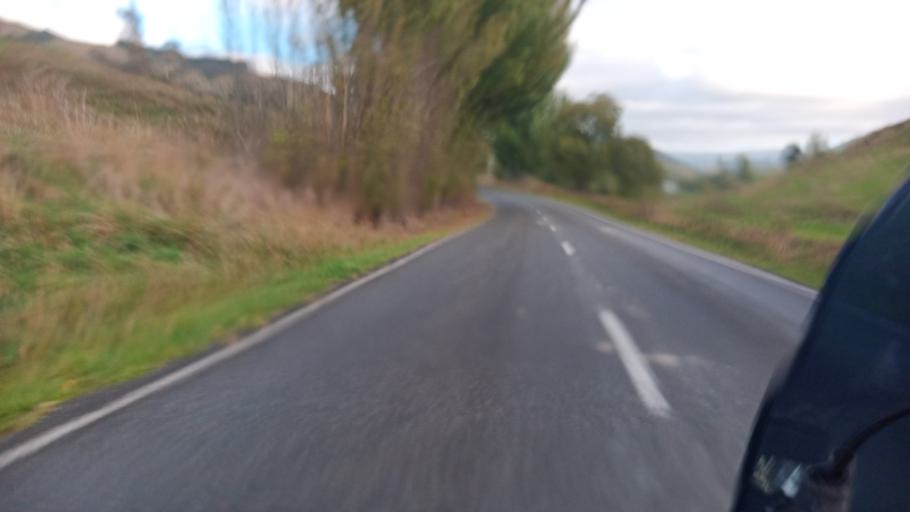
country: NZ
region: Gisborne
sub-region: Gisborne District
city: Gisborne
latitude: -38.5862
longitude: 177.7578
